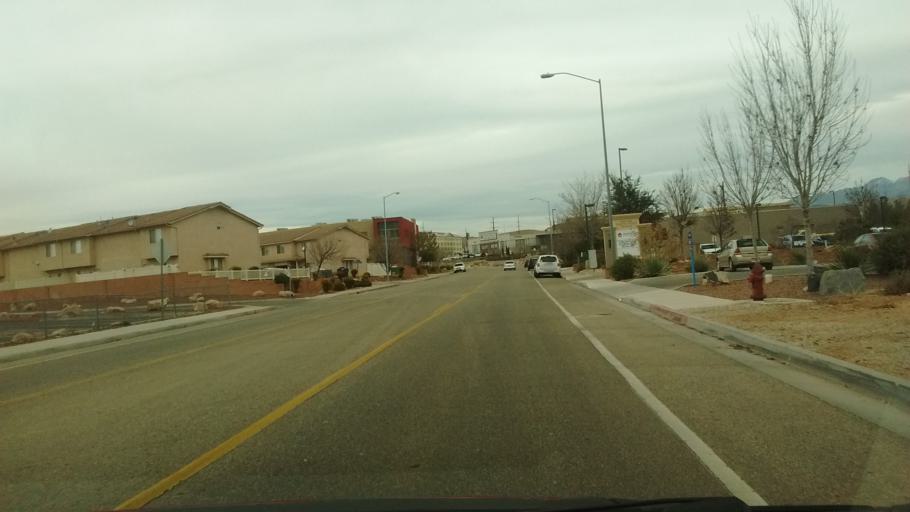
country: US
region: Utah
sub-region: Washington County
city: Washington
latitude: 37.1213
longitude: -113.5248
